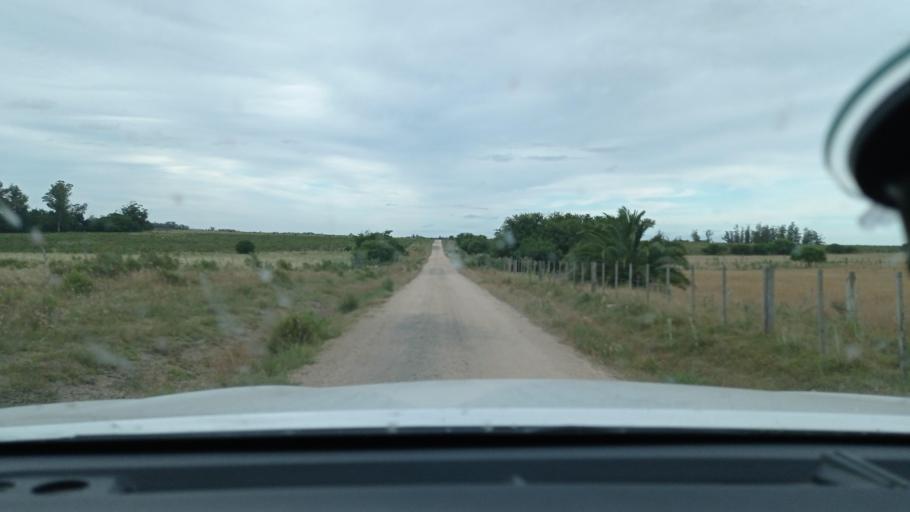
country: UY
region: Florida
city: Casupa
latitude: -34.1470
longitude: -55.7925
